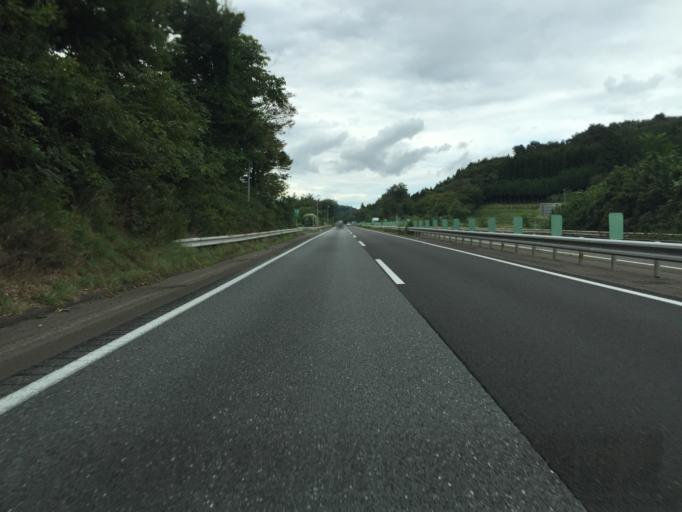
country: JP
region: Miyagi
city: Okawara
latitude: 38.1079
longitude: 140.6931
